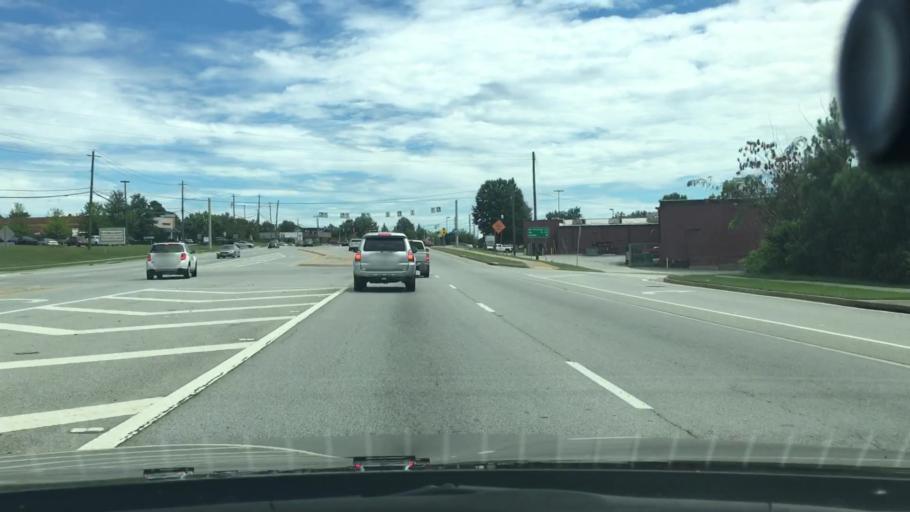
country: US
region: Georgia
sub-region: Coweta County
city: Newnan
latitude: 33.3972
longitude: -84.7643
